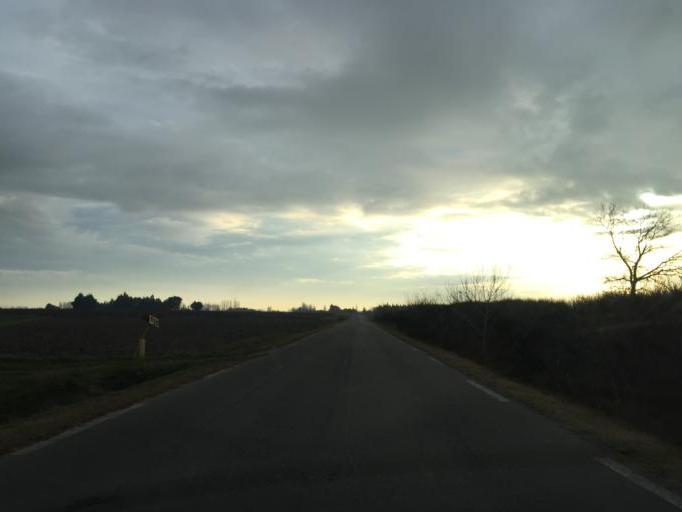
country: FR
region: Provence-Alpes-Cote d'Azur
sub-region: Departement du Vaucluse
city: Jonquieres
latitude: 44.1263
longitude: 4.8679
